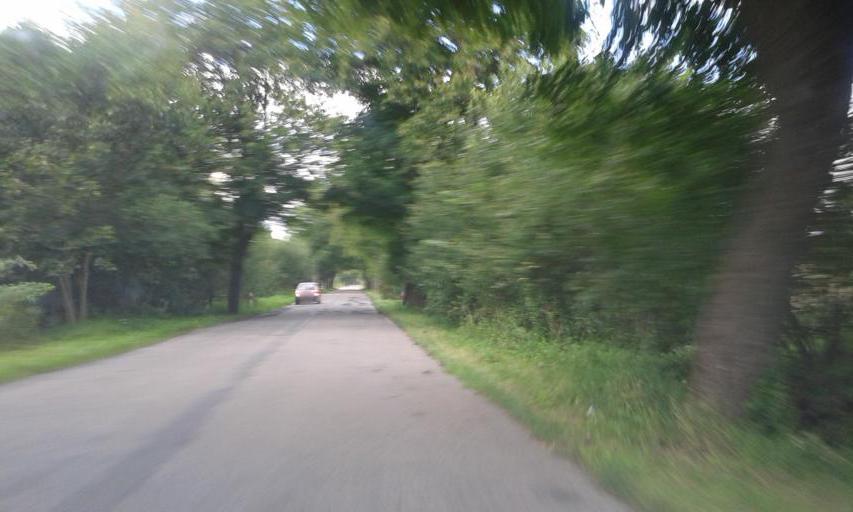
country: PL
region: West Pomeranian Voivodeship
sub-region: Powiat szczecinecki
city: Barwice
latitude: 53.7094
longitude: 16.3536
